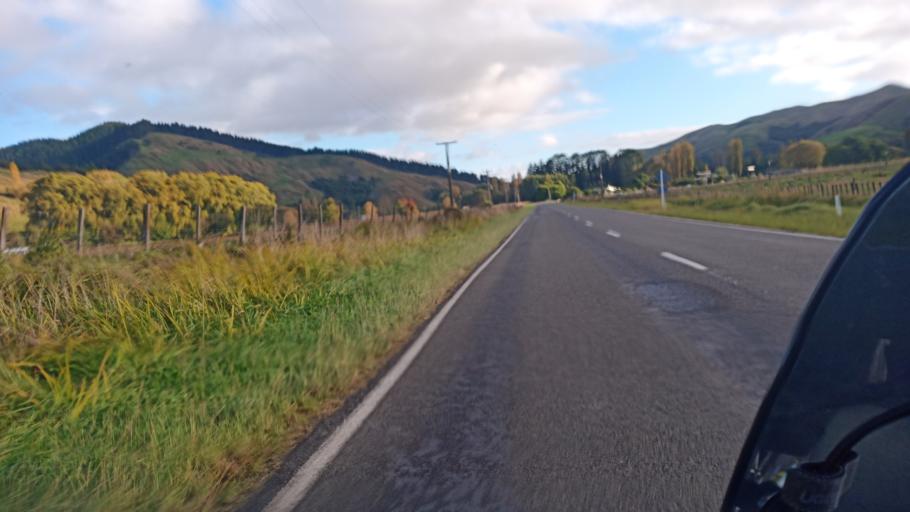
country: NZ
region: Gisborne
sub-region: Gisborne District
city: Gisborne
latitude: -38.6314
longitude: 177.8259
